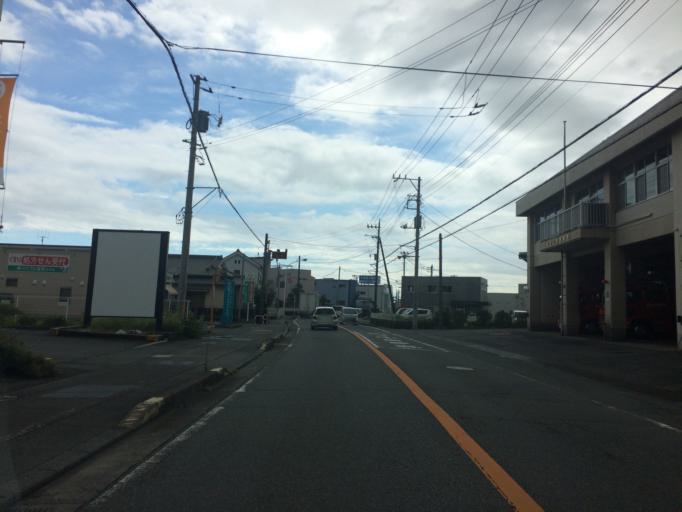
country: JP
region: Shizuoka
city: Fuji
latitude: 35.1683
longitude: 138.6488
